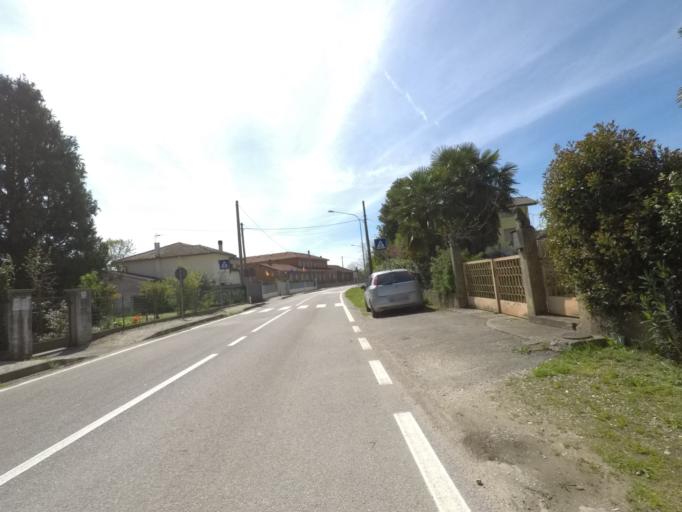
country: IT
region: Friuli Venezia Giulia
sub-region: Provincia di Pordenone
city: Casarsa della Delizia
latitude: 45.9423
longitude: 12.8427
